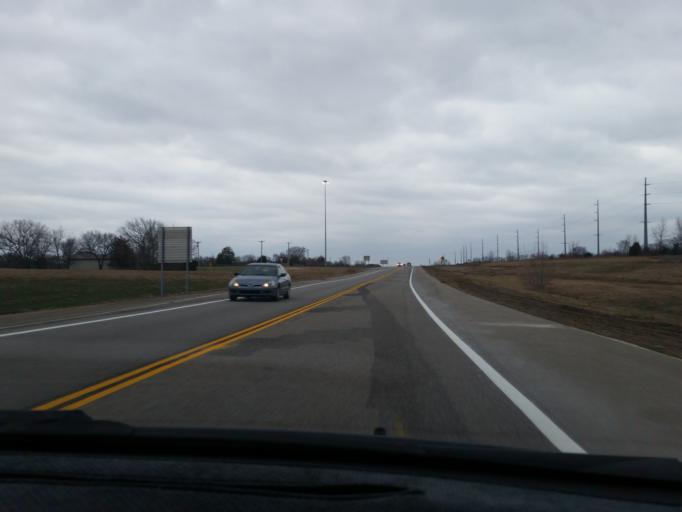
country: US
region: Kansas
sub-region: Douglas County
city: Lawrence
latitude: 38.9587
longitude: -95.3343
